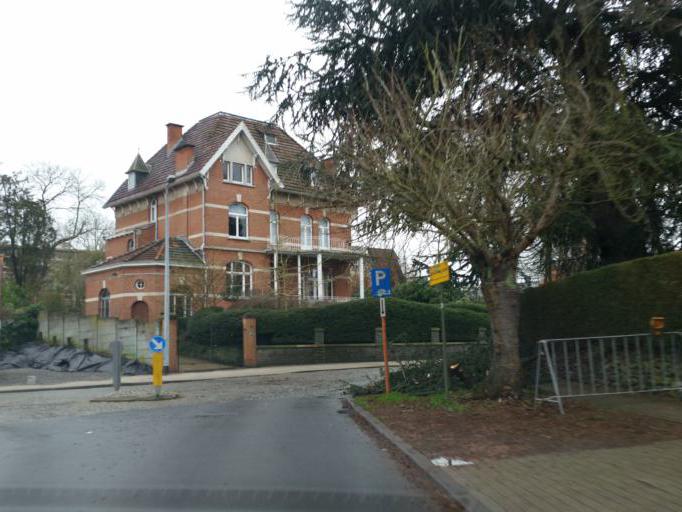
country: BE
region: Flanders
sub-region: Provincie Vlaams-Brabant
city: Grimbergen
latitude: 50.9329
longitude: 4.3666
